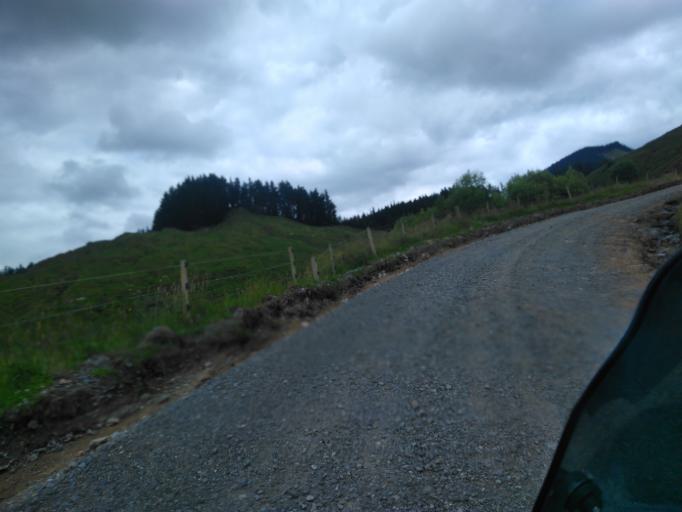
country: NZ
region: Gisborne
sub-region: Gisborne District
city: Gisborne
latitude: -38.0742
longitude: 178.0493
